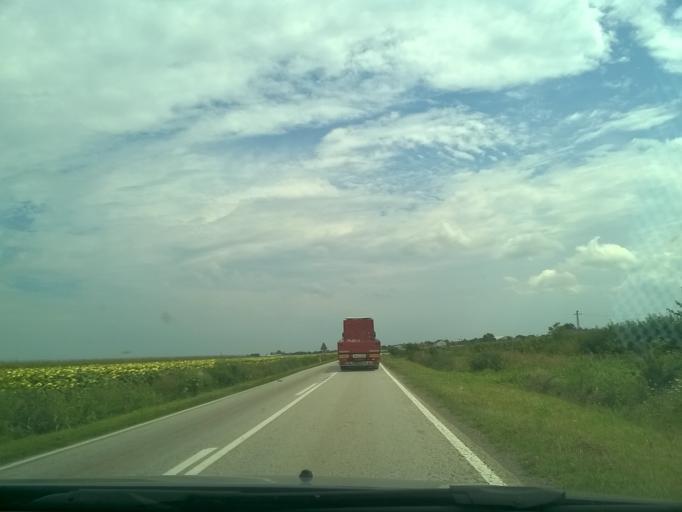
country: RS
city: Lazarevo
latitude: 45.3890
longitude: 20.5185
